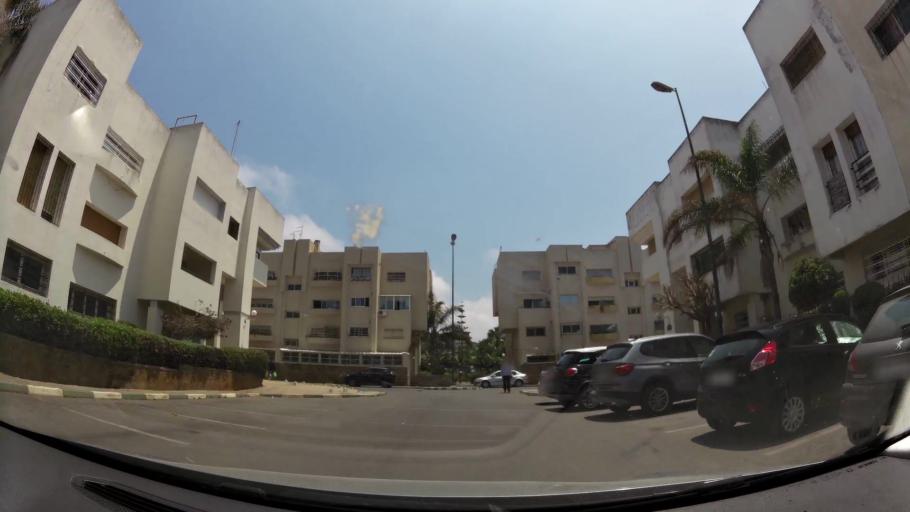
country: MA
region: Rabat-Sale-Zemmour-Zaer
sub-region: Skhirate-Temara
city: Temara
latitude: 33.9674
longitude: -6.9052
